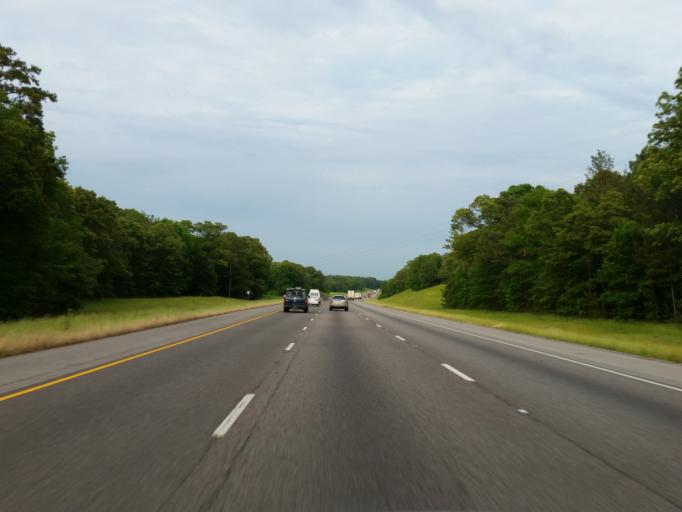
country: US
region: Alabama
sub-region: Calhoun County
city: Bynum
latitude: 33.5763
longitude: -85.9837
